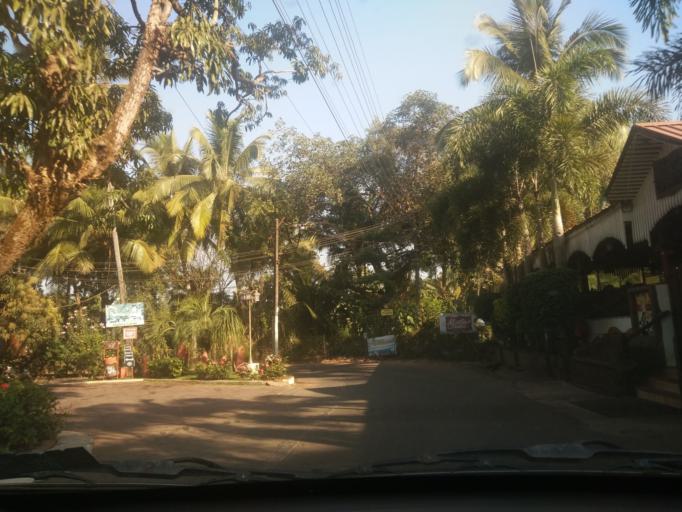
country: IN
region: Goa
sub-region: South Goa
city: Colva
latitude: 15.3037
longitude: 73.9143
